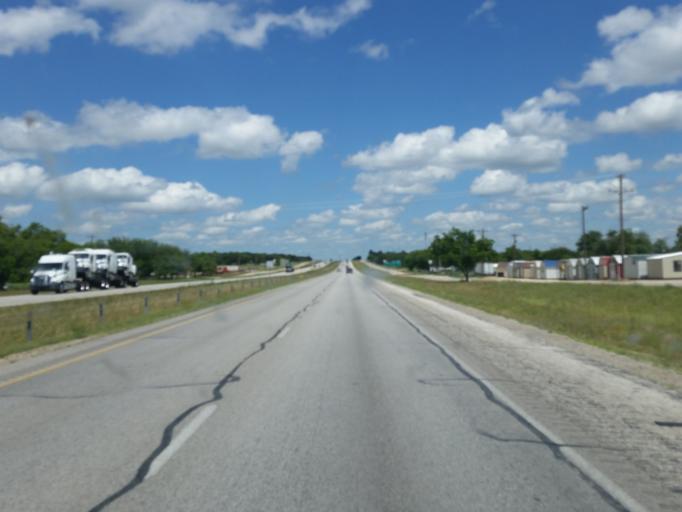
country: US
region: Texas
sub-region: Callahan County
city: Clyde
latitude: 32.4098
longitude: -99.4738
